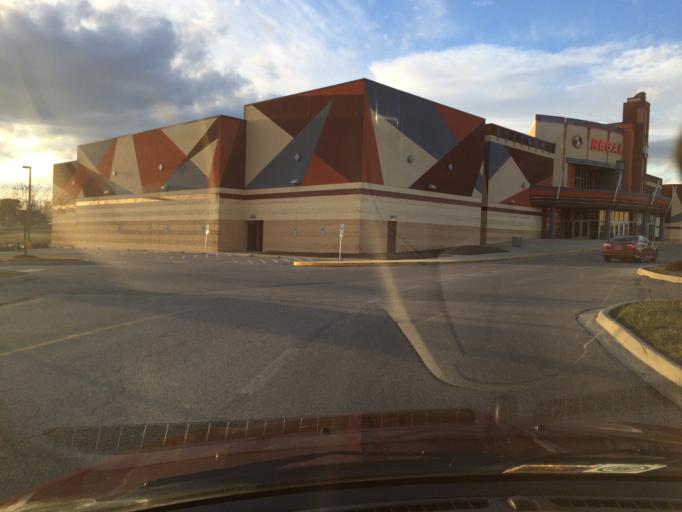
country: US
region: Virginia
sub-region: Montgomery County
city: Merrimac
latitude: 37.1633
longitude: -80.4279
